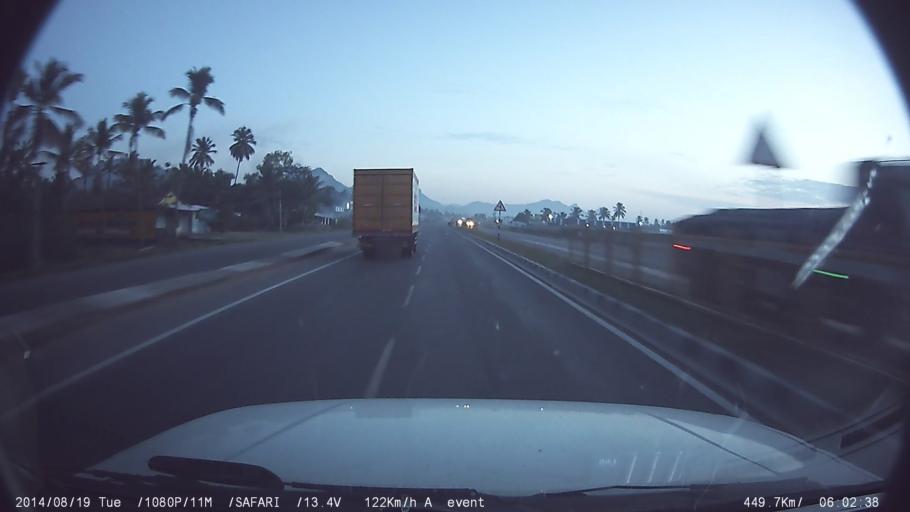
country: IN
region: Tamil Nadu
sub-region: Salem
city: Omalur
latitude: 11.8410
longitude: 78.0668
